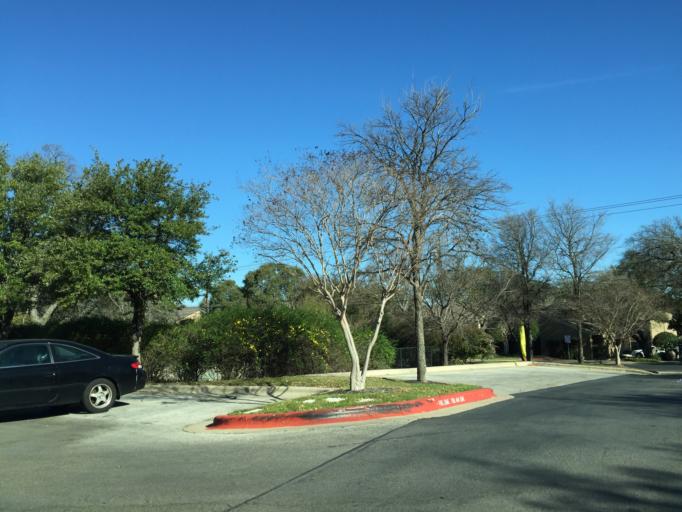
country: US
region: Texas
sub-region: Williamson County
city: Jollyville
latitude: 30.4158
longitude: -97.7444
